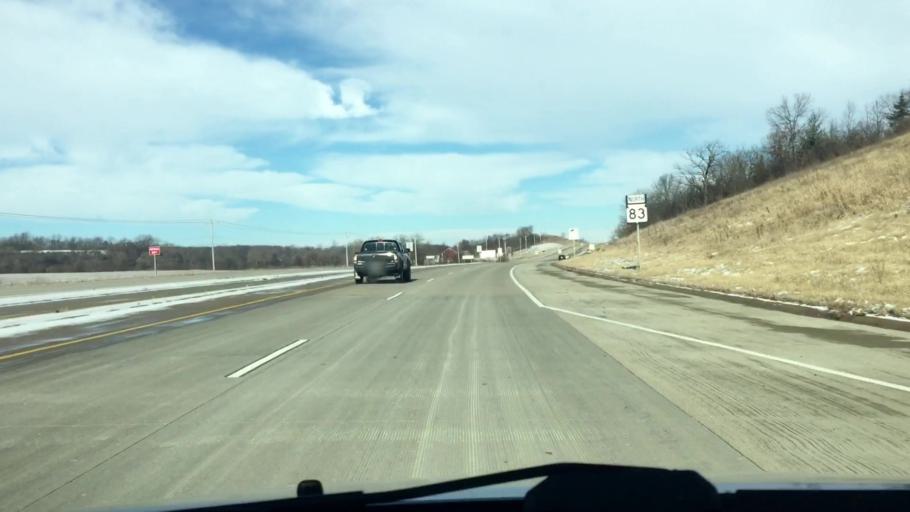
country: US
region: Wisconsin
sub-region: Waukesha County
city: Mukwonago
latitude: 42.9012
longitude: -88.3451
